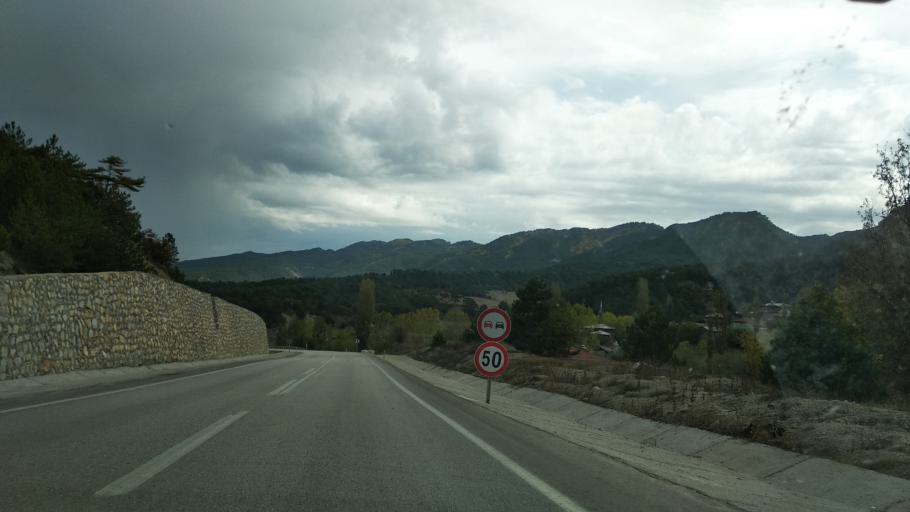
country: TR
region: Bolu
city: Mudurnu
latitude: 40.4370
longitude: 31.1546
